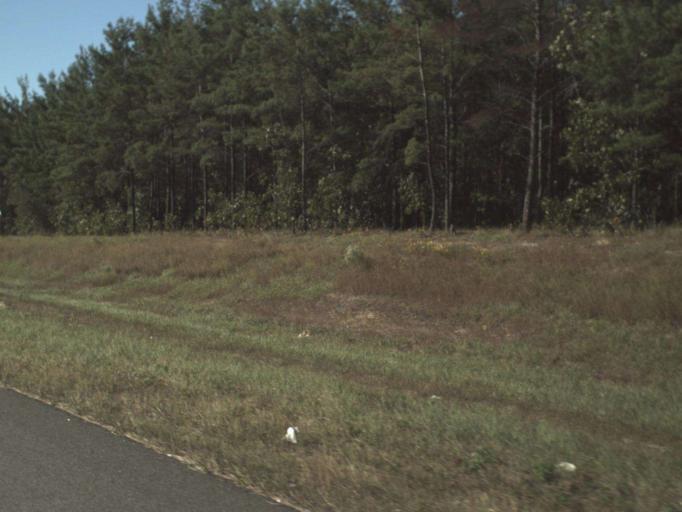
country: US
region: Florida
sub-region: Walton County
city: Freeport
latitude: 30.5174
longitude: -86.1100
